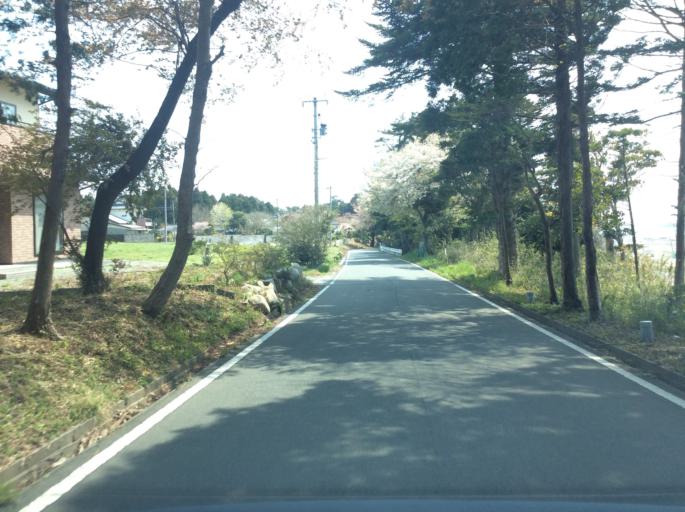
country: JP
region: Fukushima
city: Namie
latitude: 37.2708
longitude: 141.0090
